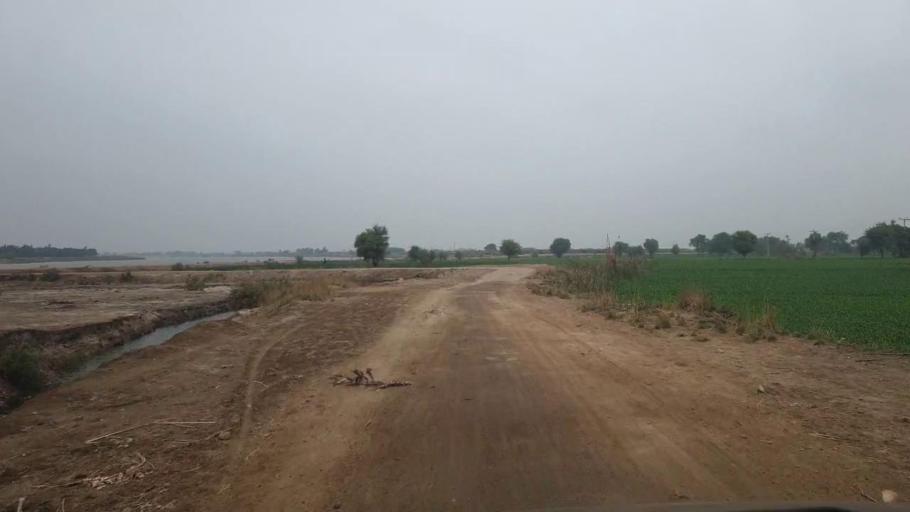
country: PK
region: Sindh
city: Tando Adam
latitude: 25.8551
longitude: 68.7029
